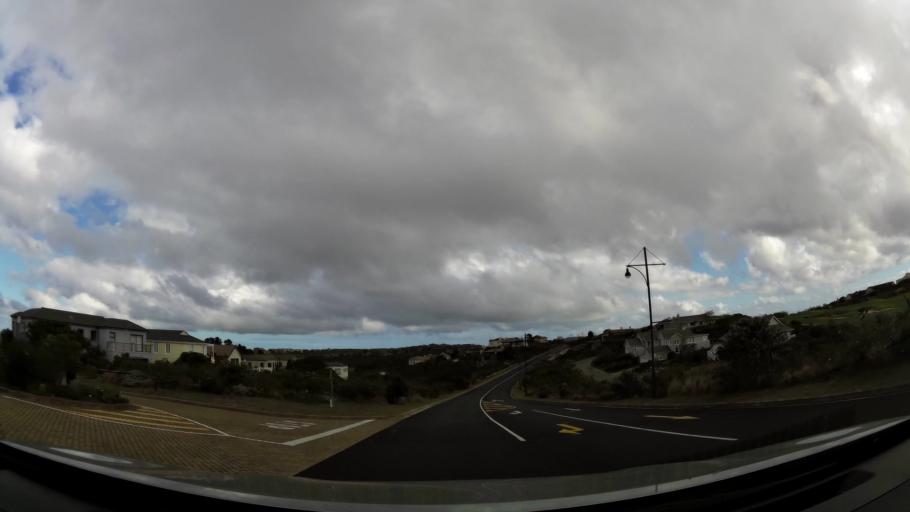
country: ZA
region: Western Cape
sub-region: Eden District Municipality
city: Knysna
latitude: -34.0671
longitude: 23.0984
